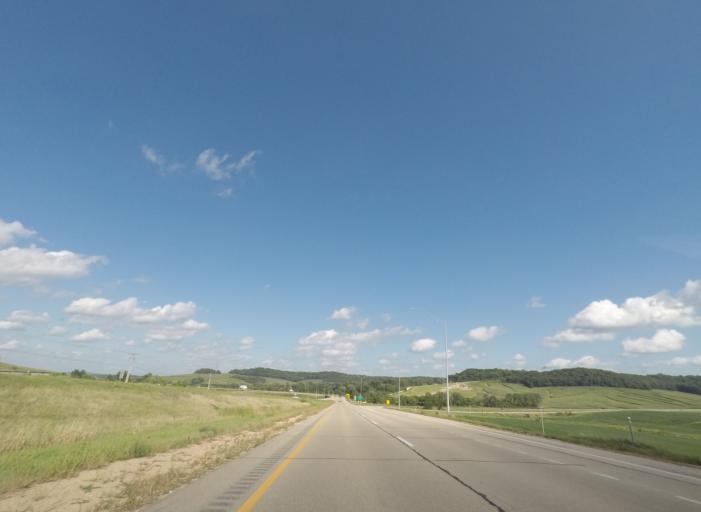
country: US
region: Iowa
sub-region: Dubuque County
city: Dubuque
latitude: 42.4187
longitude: -90.7014
